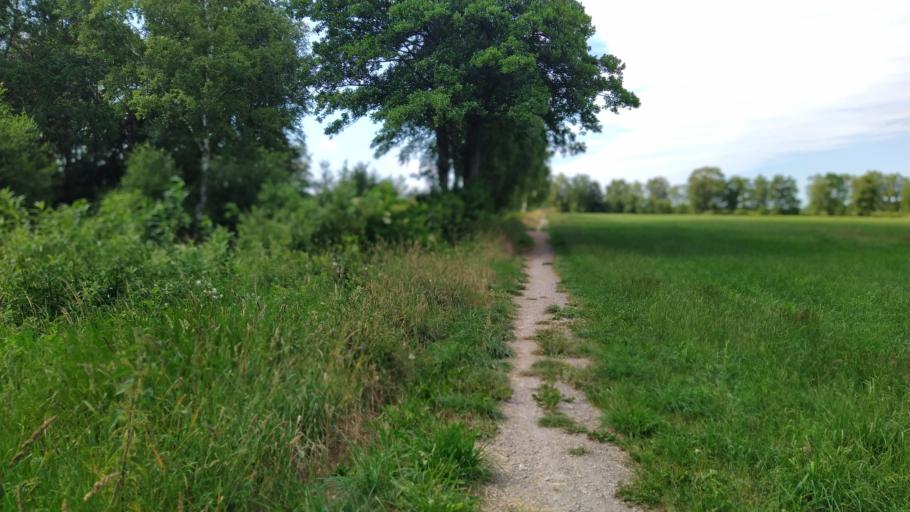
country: DE
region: Lower Saxony
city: Stinstedt
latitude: 53.6423
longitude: 8.9502
